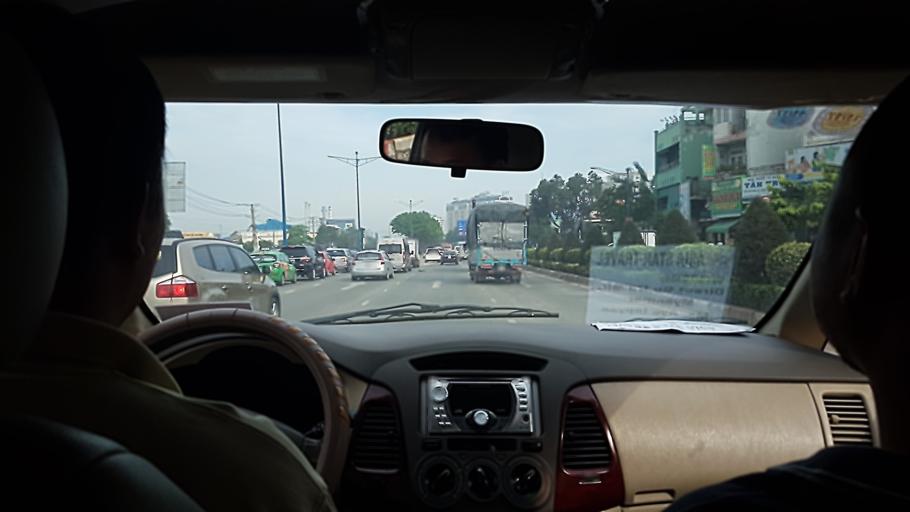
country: VN
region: Ho Chi Minh City
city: Ho Chi Minh City
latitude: 10.8196
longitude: 106.6310
